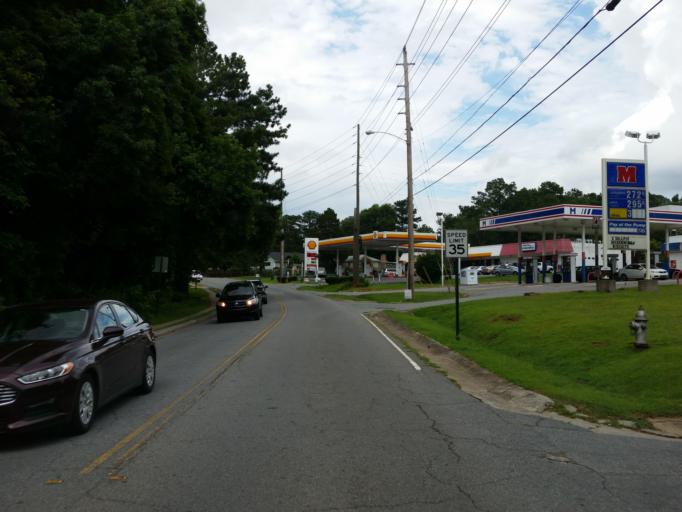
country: US
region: Georgia
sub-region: Cobb County
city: Kennesaw
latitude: 34.0338
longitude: -84.6061
